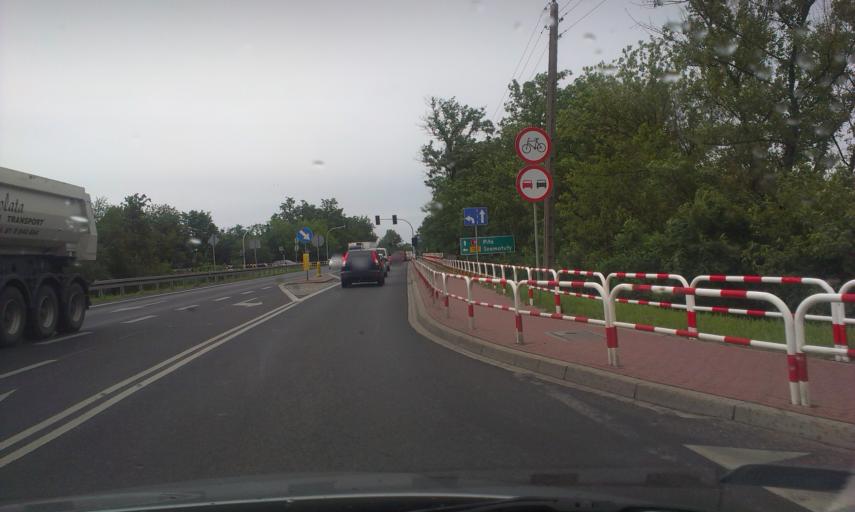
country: PL
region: Greater Poland Voivodeship
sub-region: Powiat obornicki
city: Oborniki
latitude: 52.6410
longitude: 16.8130
